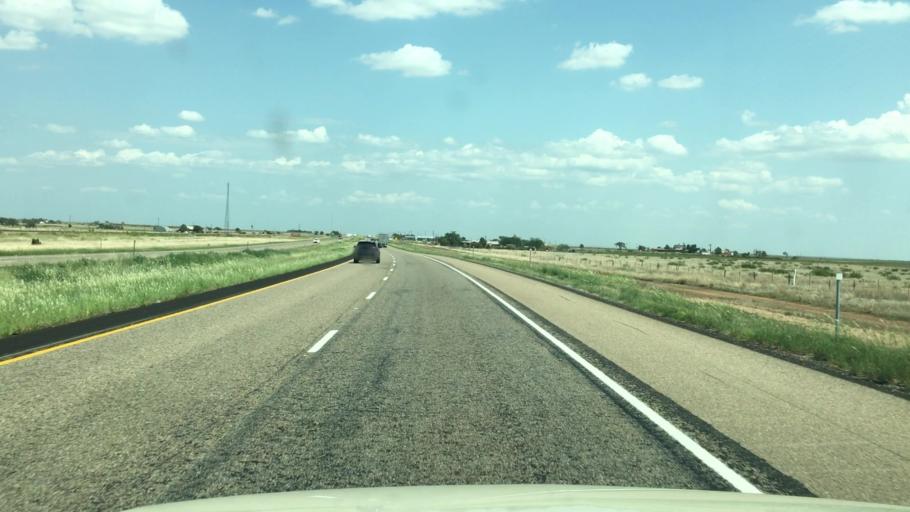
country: US
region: Texas
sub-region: Armstrong County
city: Claude
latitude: 35.0344
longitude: -101.1945
